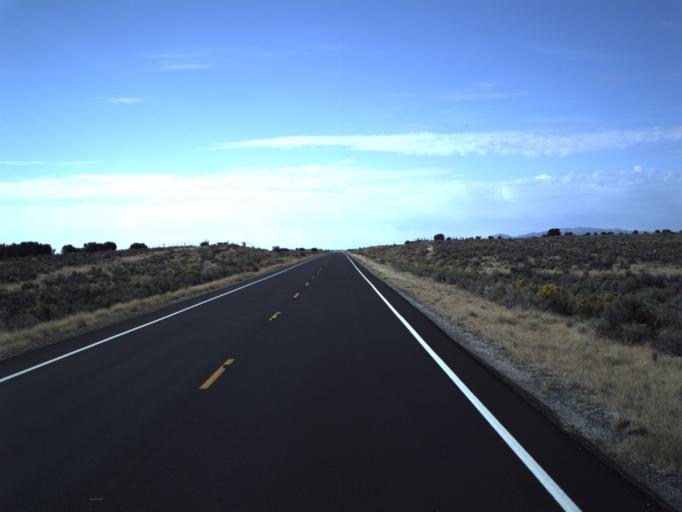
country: US
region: Idaho
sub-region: Cassia County
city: Burley
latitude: 41.7159
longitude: -113.5282
